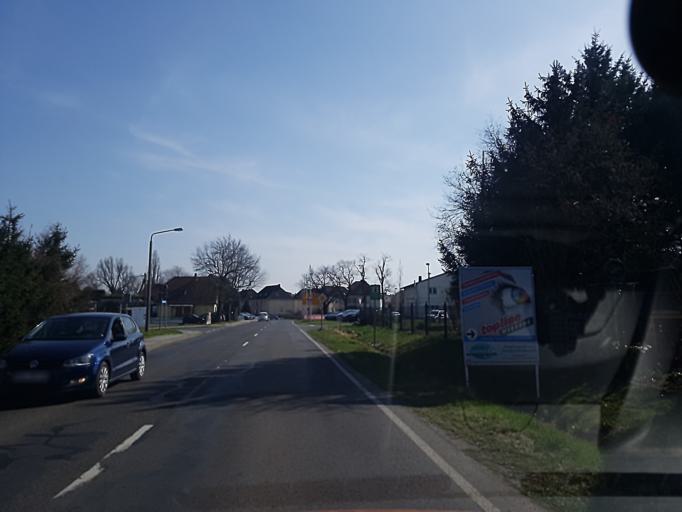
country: DE
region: Brandenburg
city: Calau
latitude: 51.7475
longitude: 13.9447
